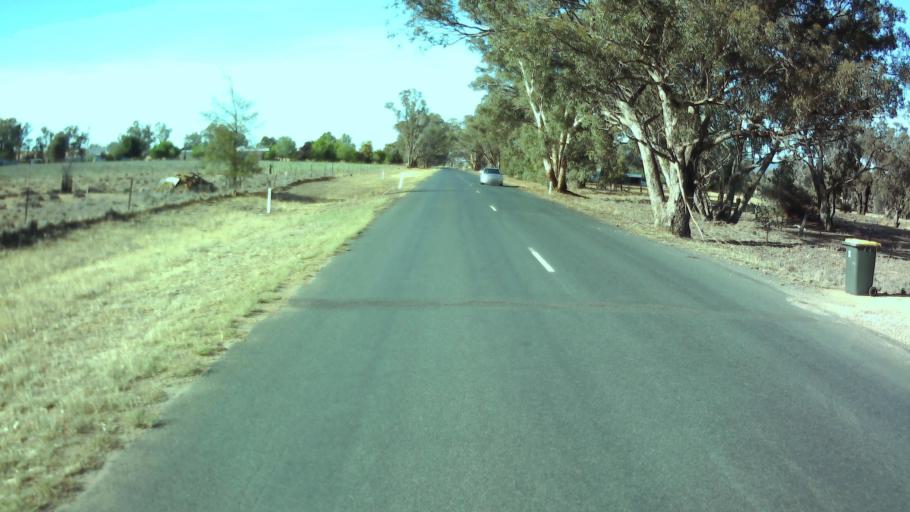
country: AU
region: New South Wales
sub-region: Weddin
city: Grenfell
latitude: -33.9121
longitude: 148.1441
